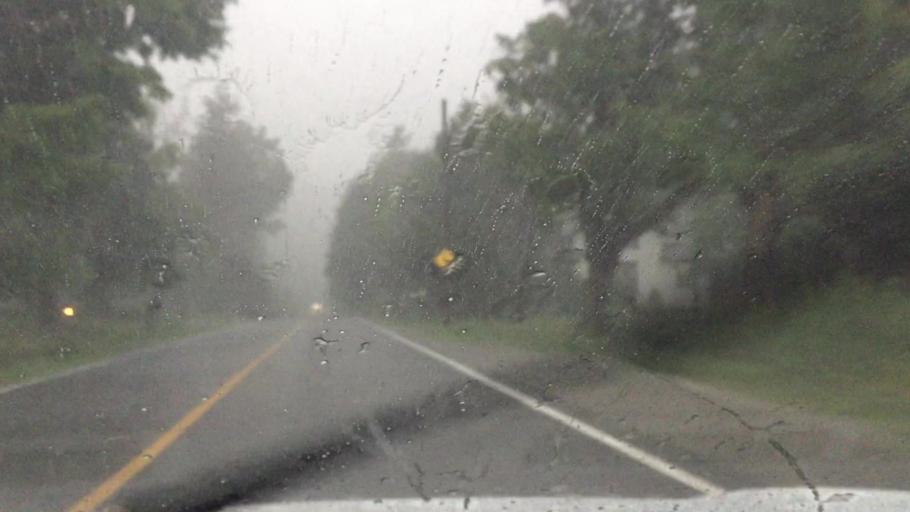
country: CA
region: Ontario
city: Markham
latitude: 43.8574
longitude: -79.2039
